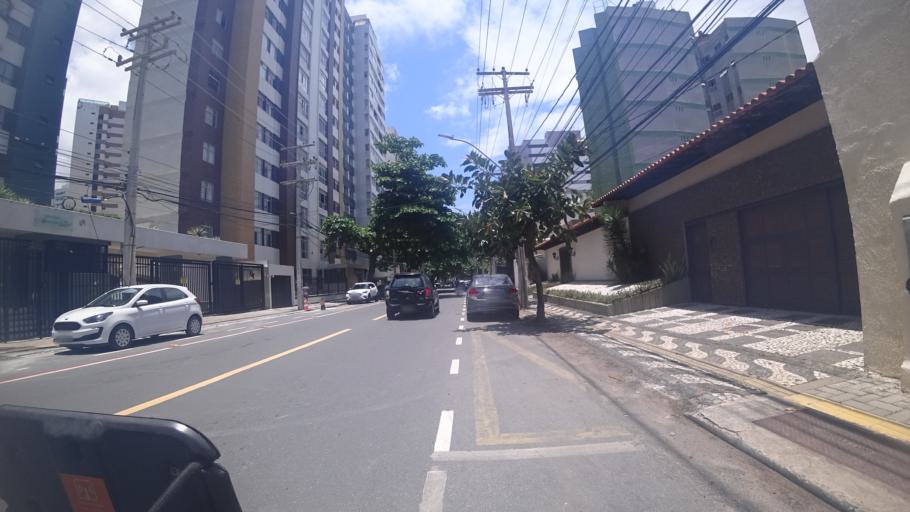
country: BR
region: Bahia
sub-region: Salvador
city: Salvador
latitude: -13.0086
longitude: -38.4662
